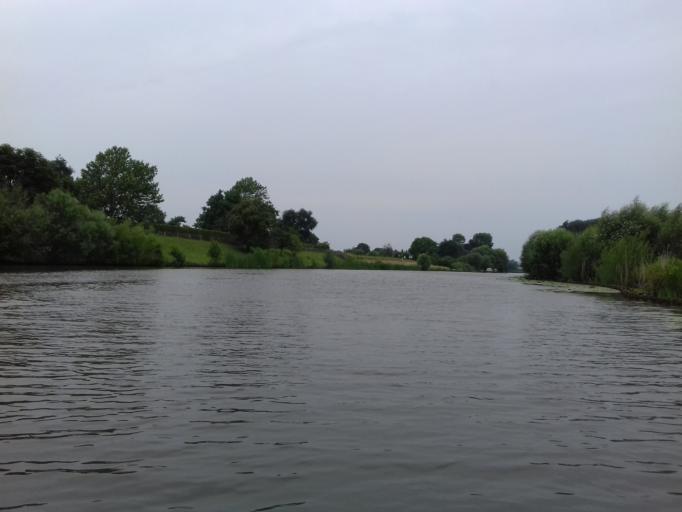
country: NL
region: Gelderland
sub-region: Gemeente Geldermalsen
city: Geldermalsen
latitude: 51.8862
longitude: 5.2198
